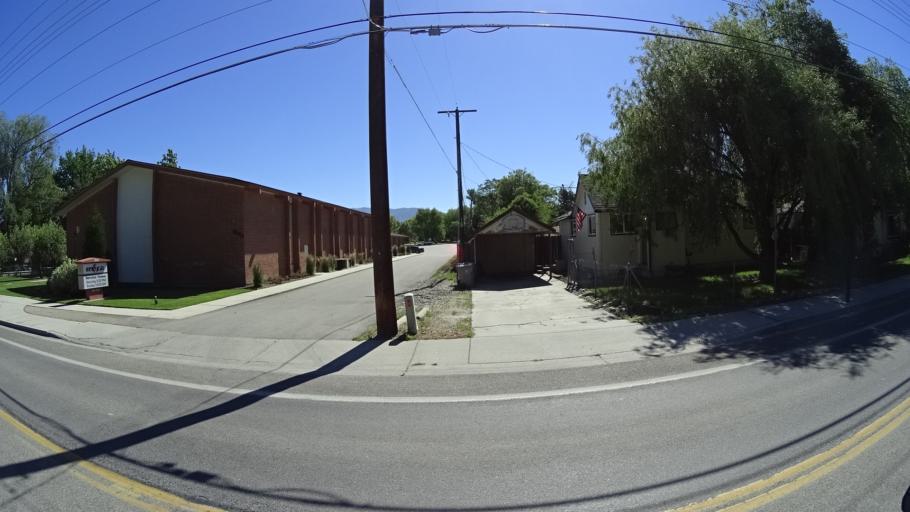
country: US
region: Idaho
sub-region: Ada County
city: Garden City
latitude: 43.6436
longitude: -116.2334
